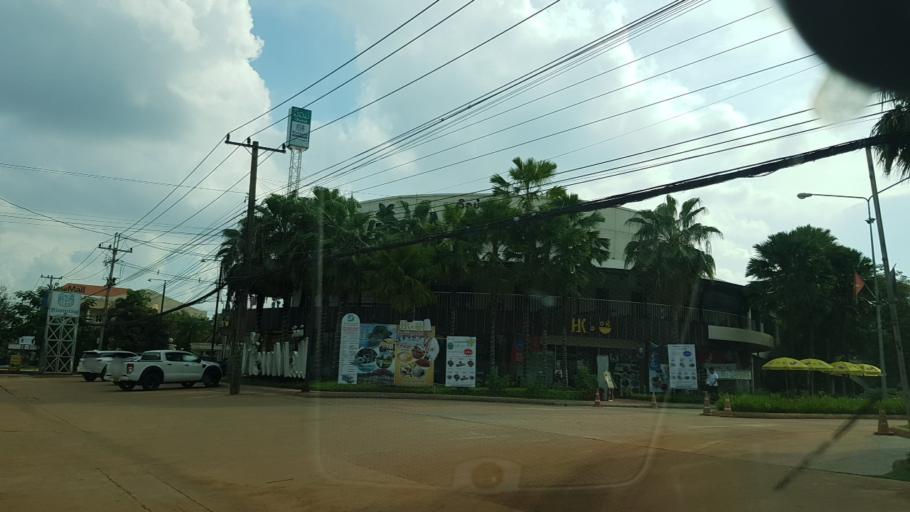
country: LA
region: Vientiane
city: Vientiane
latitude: 18.0160
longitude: 102.6499
